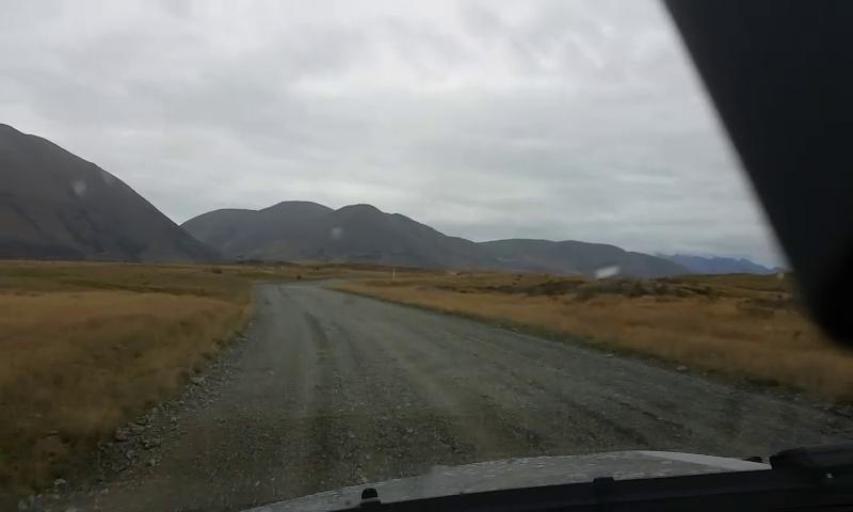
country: NZ
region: Canterbury
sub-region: Ashburton District
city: Methven
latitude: -43.6149
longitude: 171.1080
